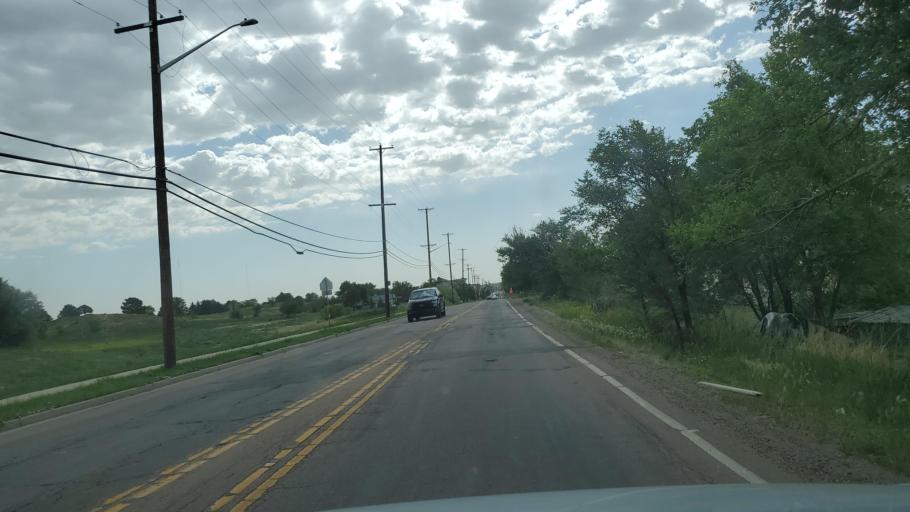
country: US
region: Colorado
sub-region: Adams County
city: Welby
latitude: 39.8381
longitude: -104.9715
